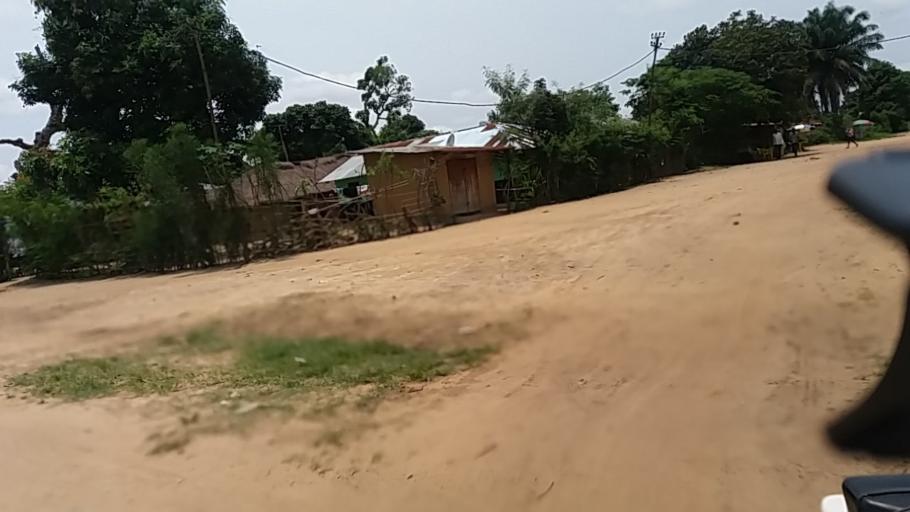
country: CD
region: Bandundu
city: Bandundu
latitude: -3.3233
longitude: 17.3954
